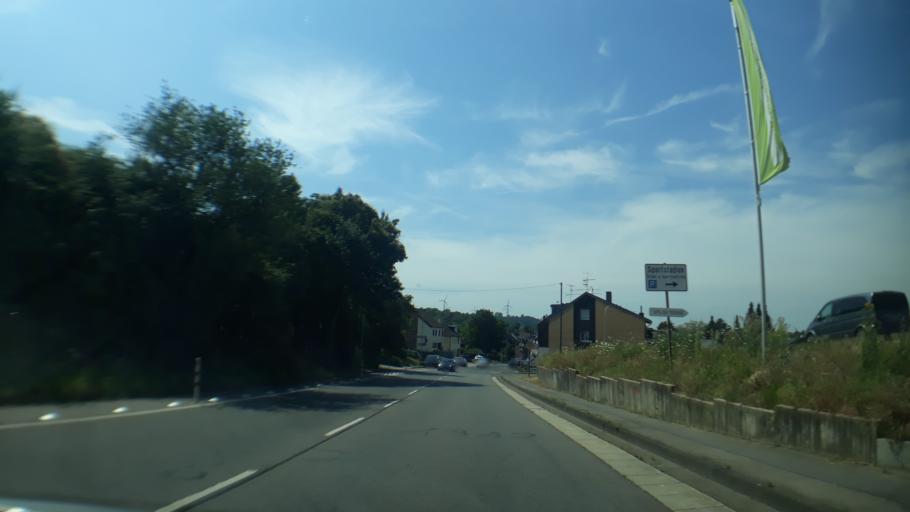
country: DE
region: North Rhine-Westphalia
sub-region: Regierungsbezirk Koln
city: Langerwehe
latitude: 50.8165
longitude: 6.3706
